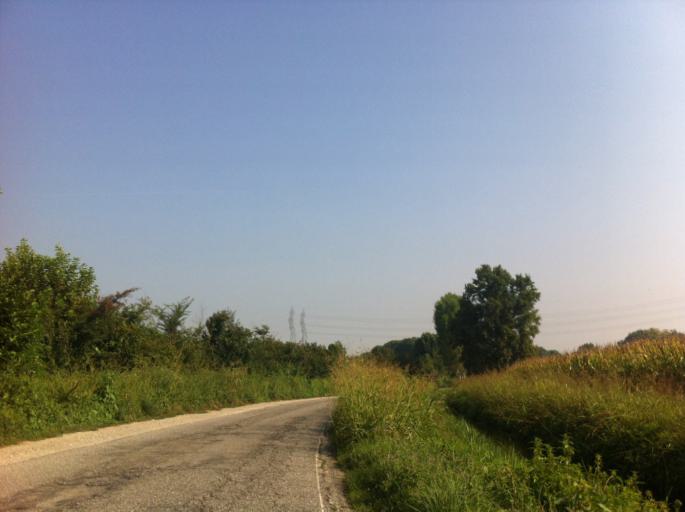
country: IT
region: Lombardy
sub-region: Provincia di Lodi
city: Tavazzano
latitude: 45.3419
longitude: 9.4117
